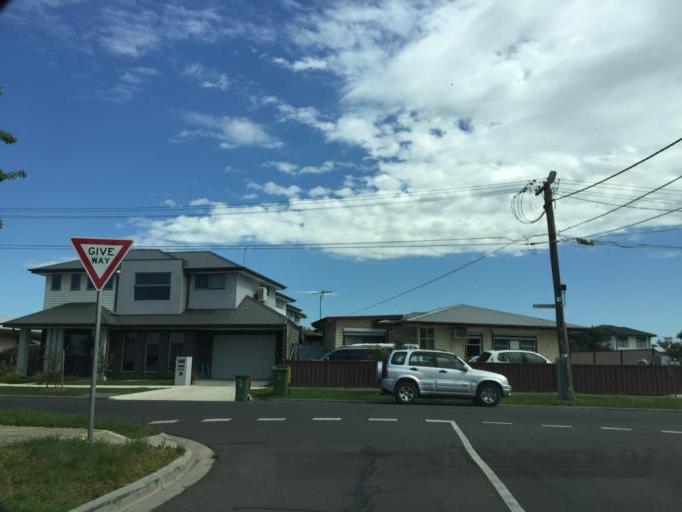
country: AU
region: Victoria
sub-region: Maribyrnong
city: Braybrook
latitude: -37.7832
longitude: 144.8620
